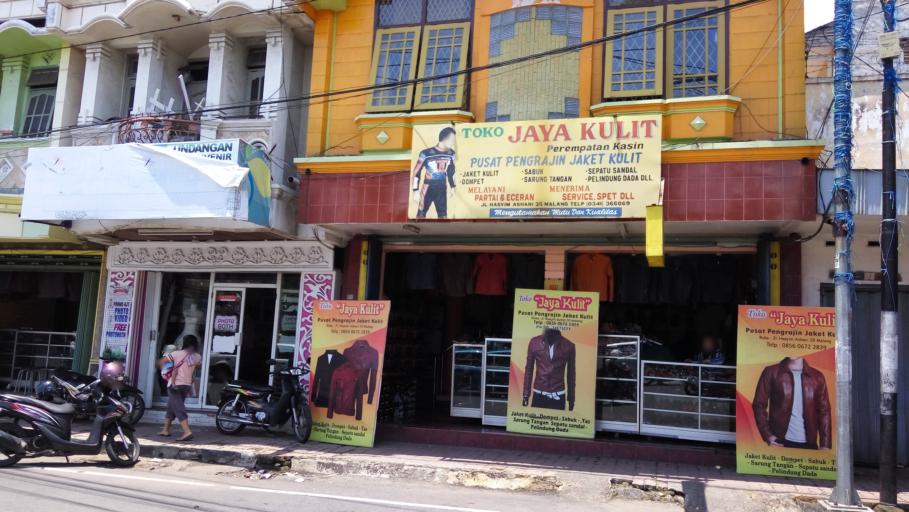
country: ID
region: East Java
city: Malang
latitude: -7.9839
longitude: 112.6263
